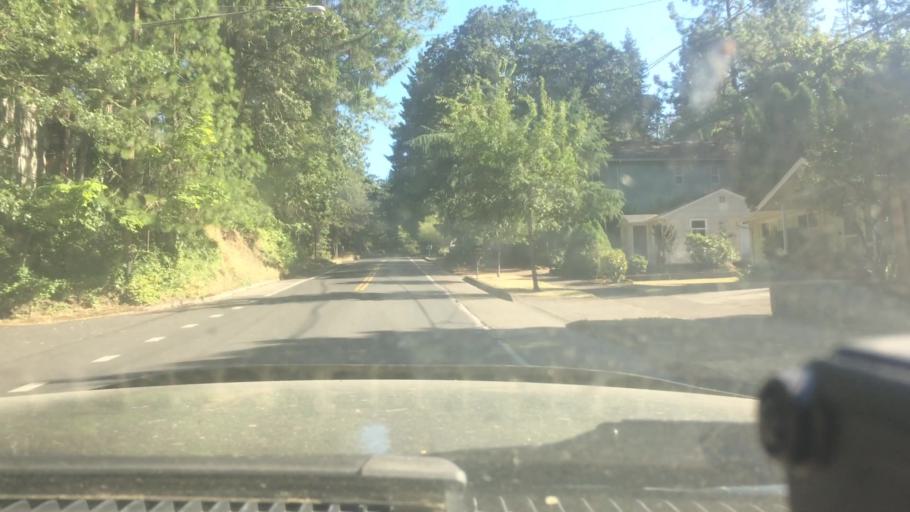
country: US
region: Oregon
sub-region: Lane County
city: Eugene
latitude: 44.0095
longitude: -123.0787
